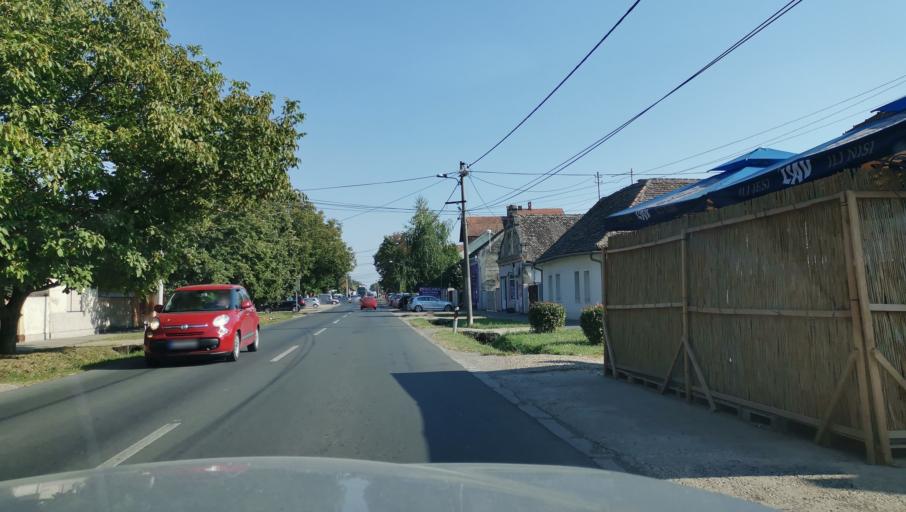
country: RS
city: Dobanovci
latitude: 44.8294
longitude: 20.2215
